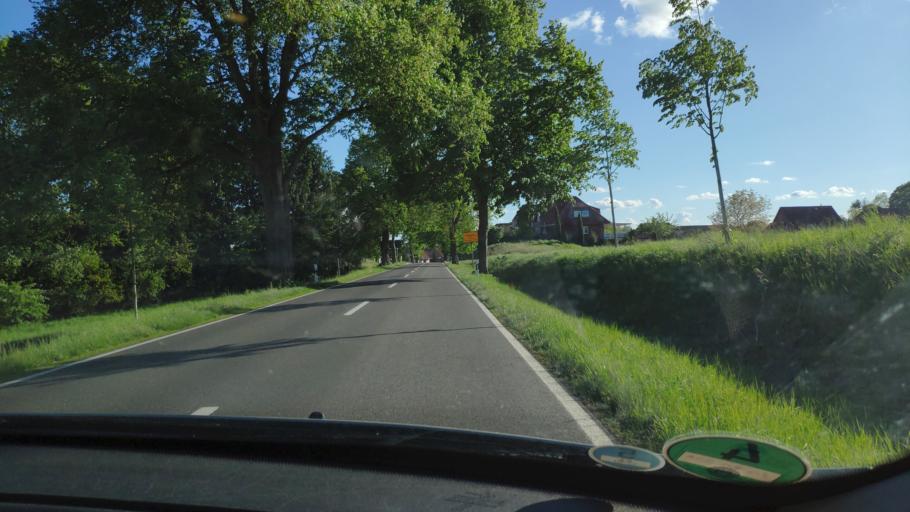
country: DE
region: Mecklenburg-Vorpommern
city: Wesenberg
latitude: 53.3422
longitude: 12.9843
